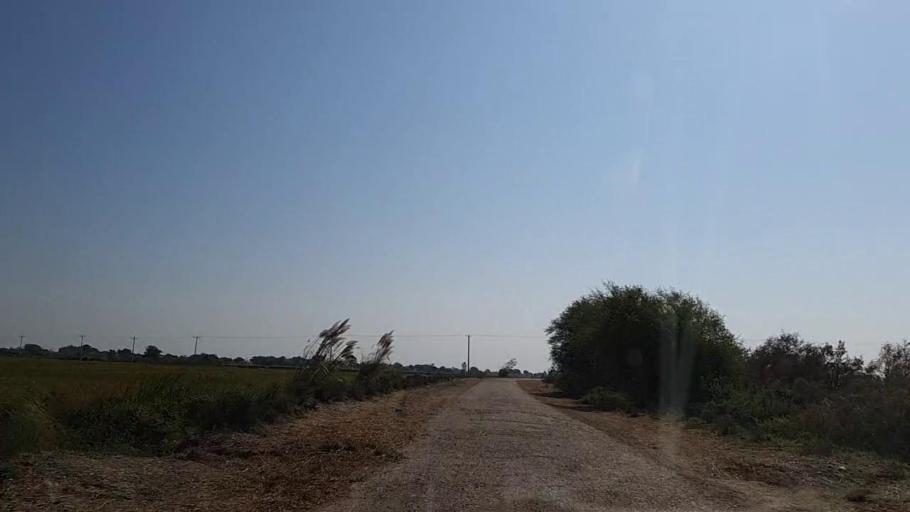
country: PK
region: Sindh
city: Chuhar Jamali
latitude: 24.5223
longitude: 68.0922
